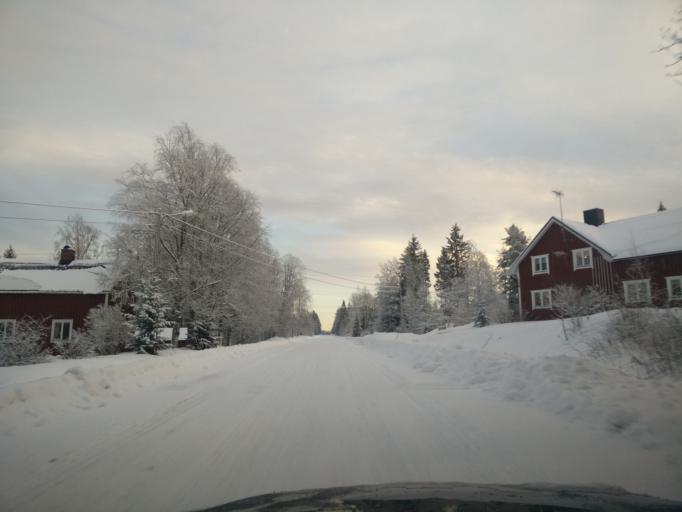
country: SE
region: Vaesternorrland
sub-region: Sundsvalls Kommun
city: Njurundabommen
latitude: 62.2196
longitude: 17.3586
